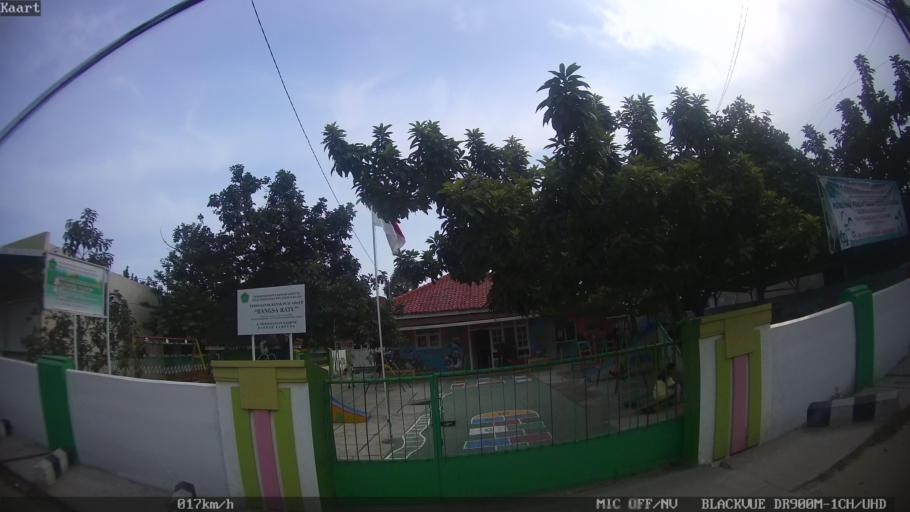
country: ID
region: Lampung
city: Kedaton
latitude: -5.3970
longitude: 105.3022
